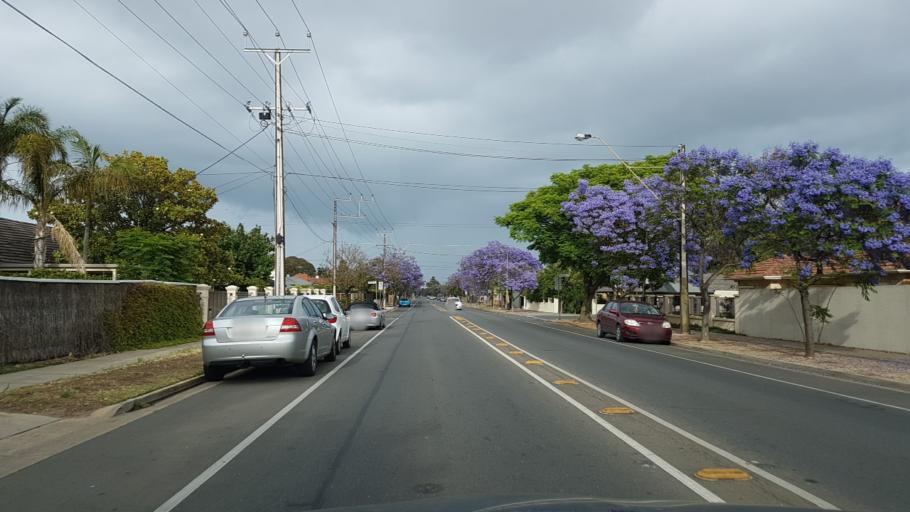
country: AU
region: South Australia
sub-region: City of West Torrens
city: Plympton
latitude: -34.9599
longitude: 138.5517
